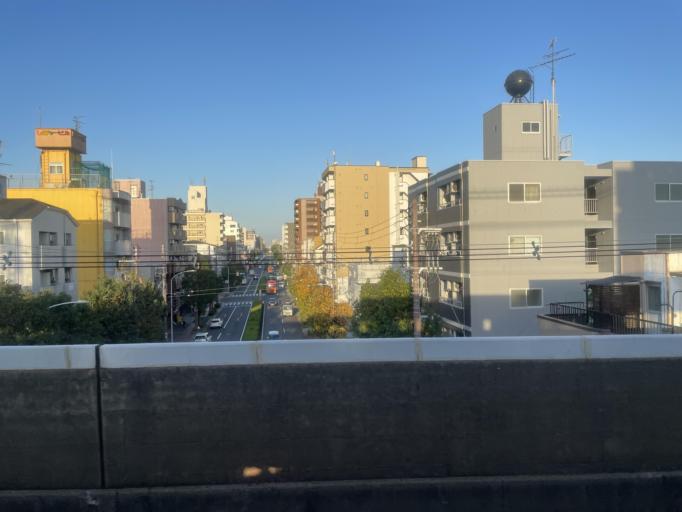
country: JP
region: Osaka
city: Matsubara
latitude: 34.6094
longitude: 135.5333
